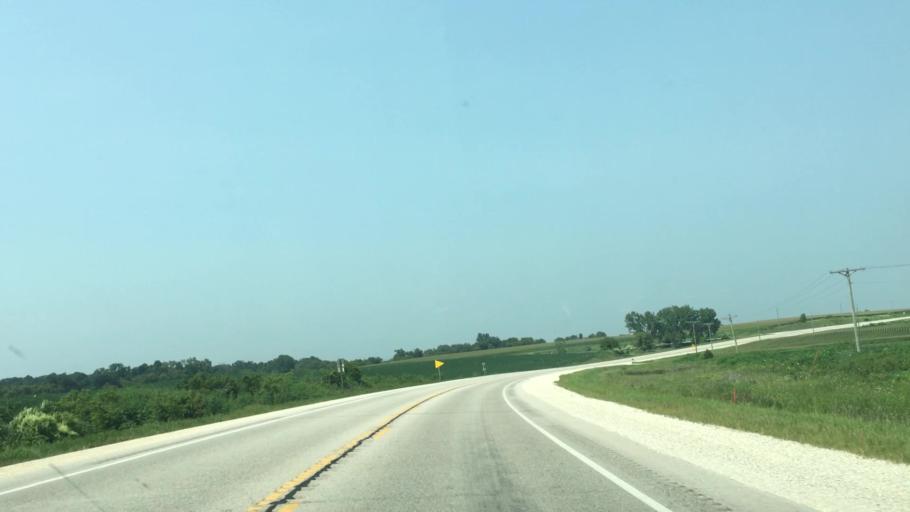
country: US
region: Iowa
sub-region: Winneshiek County
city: Decorah
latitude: 43.2077
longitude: -91.8798
